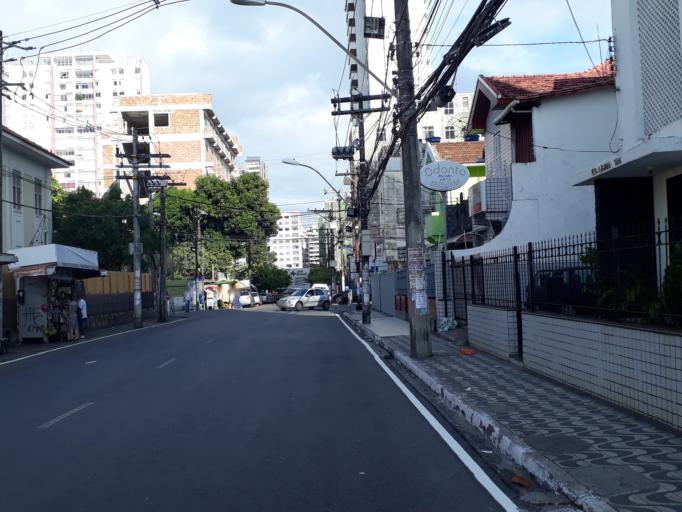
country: BR
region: Bahia
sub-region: Salvador
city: Salvador
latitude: -12.9922
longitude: -38.5212
